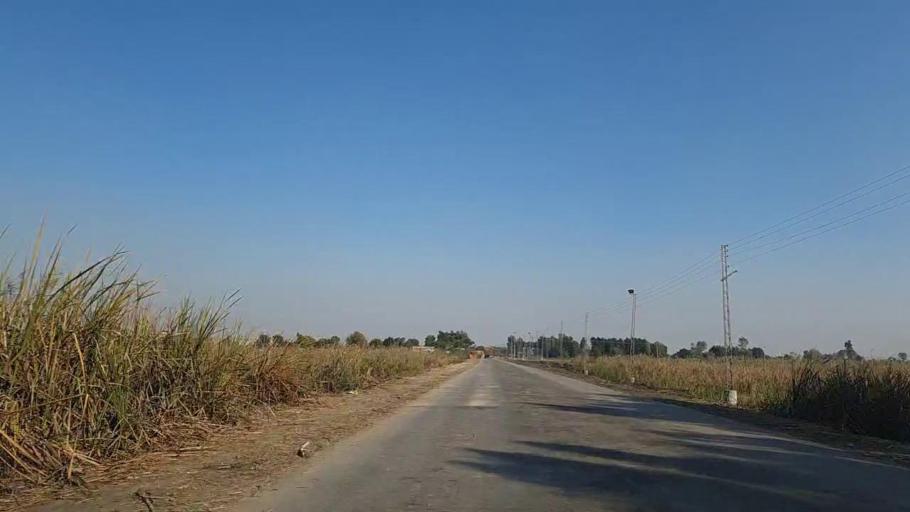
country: PK
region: Sindh
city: Bandhi
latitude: 26.6053
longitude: 68.3092
